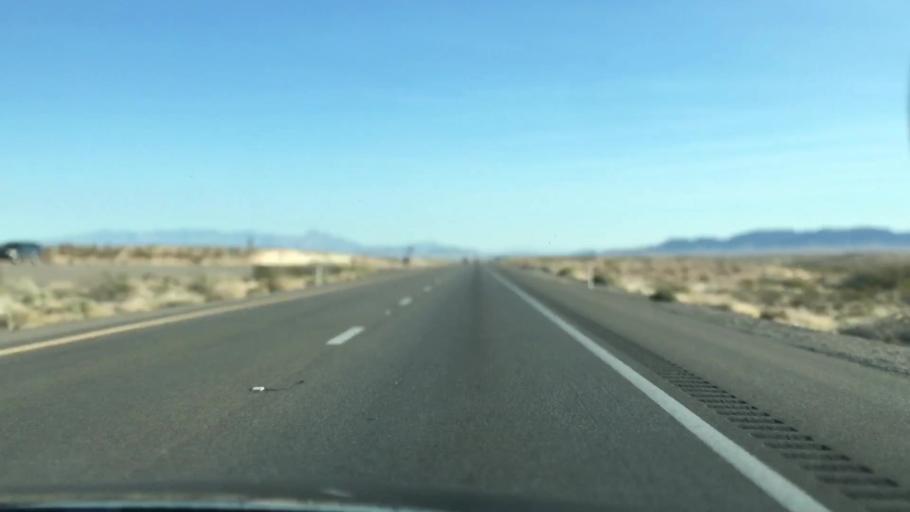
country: US
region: Nevada
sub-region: Clark County
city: Moapa Town
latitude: 36.5196
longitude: -114.7374
